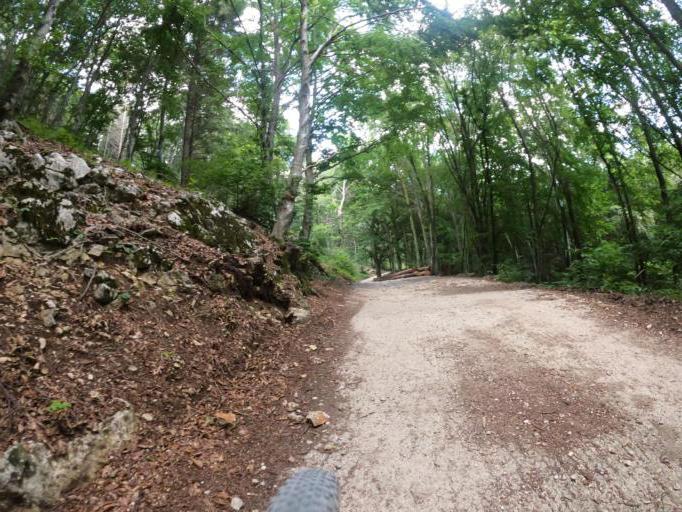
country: IT
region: Veneto
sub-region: Provincia di Verona
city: Ferrara di Monte Baldo
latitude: 45.6560
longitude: 10.8289
